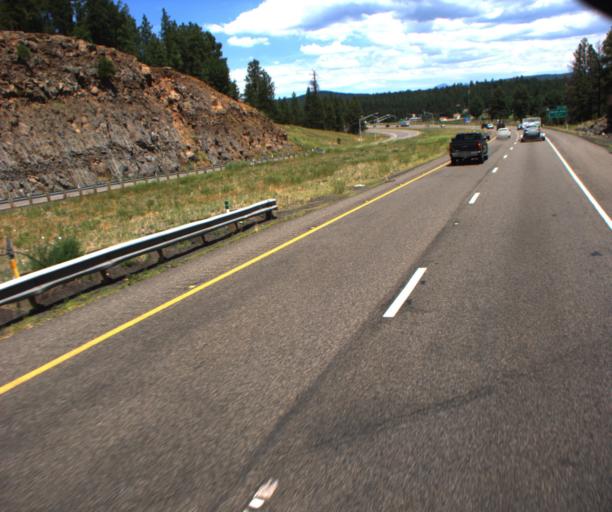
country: US
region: Arizona
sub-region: Coconino County
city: Sedona
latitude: 34.9335
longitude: -111.6493
